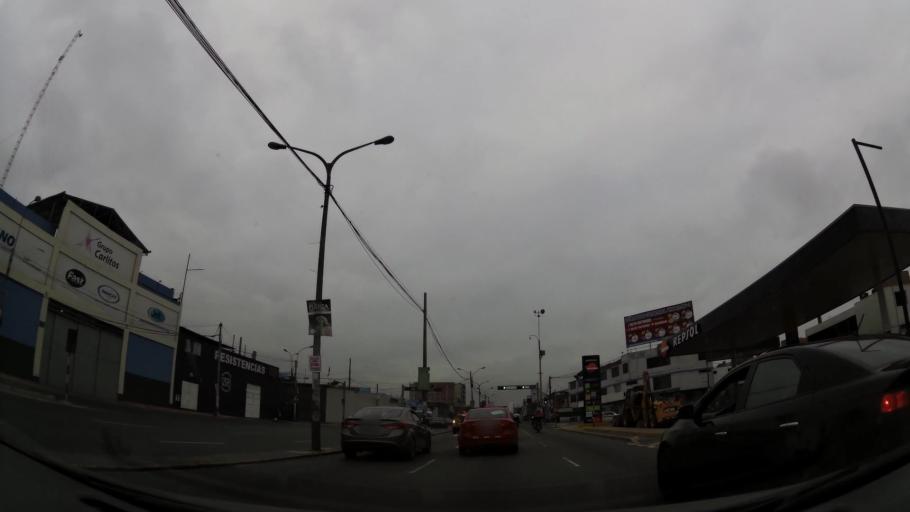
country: PE
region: Lima
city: Lima
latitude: -12.0486
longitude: -77.0654
